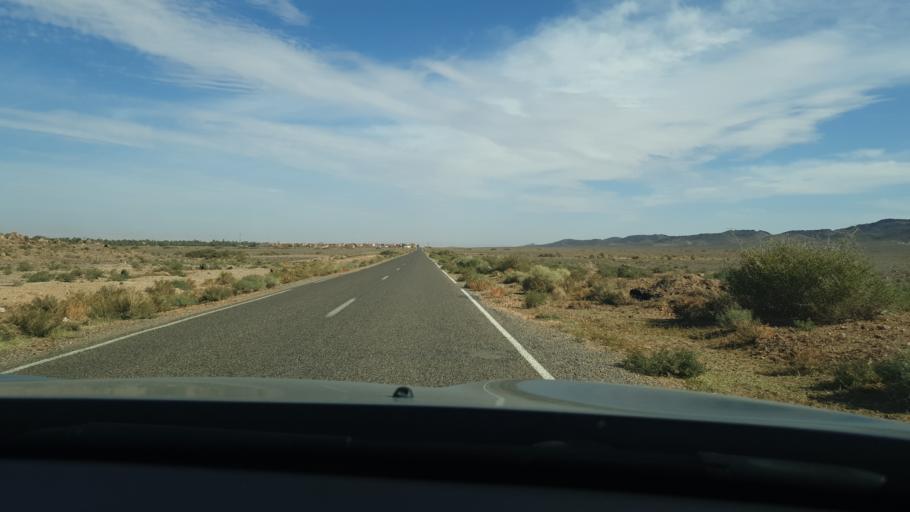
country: MA
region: Meknes-Tafilalet
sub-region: Errachidia
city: Goulmima
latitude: 31.5167
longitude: -4.9820
